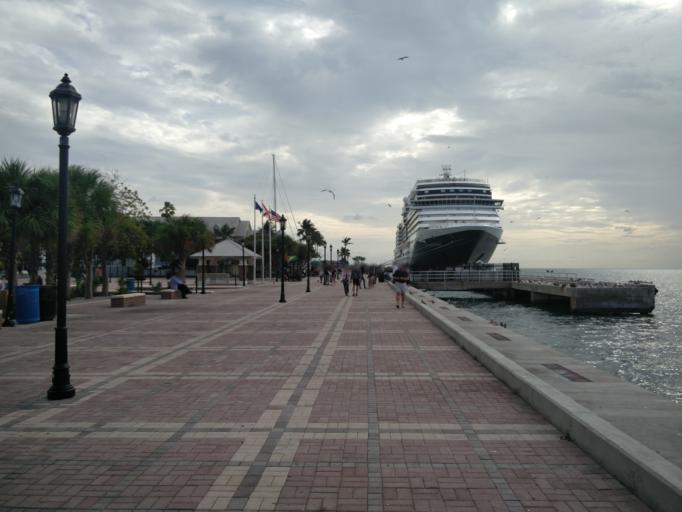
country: US
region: Florida
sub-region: Monroe County
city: Key West
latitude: 24.5605
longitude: -81.8077
